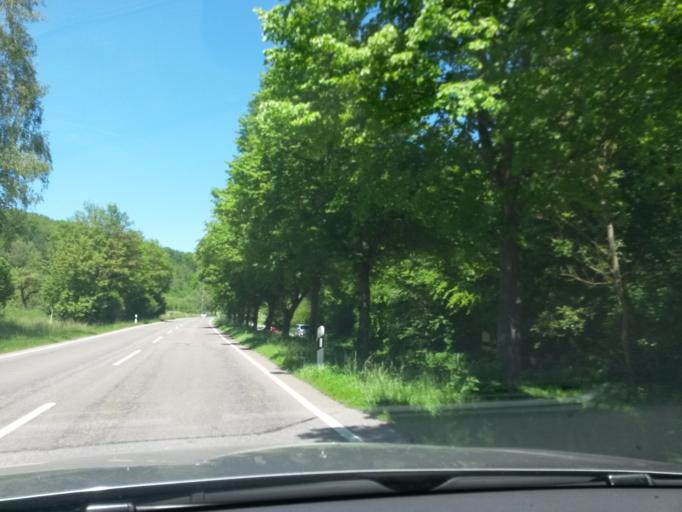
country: DE
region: Baden-Wuerttemberg
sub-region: Regierungsbezirk Stuttgart
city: Weil der Stadt
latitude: 48.7377
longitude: 8.8755
